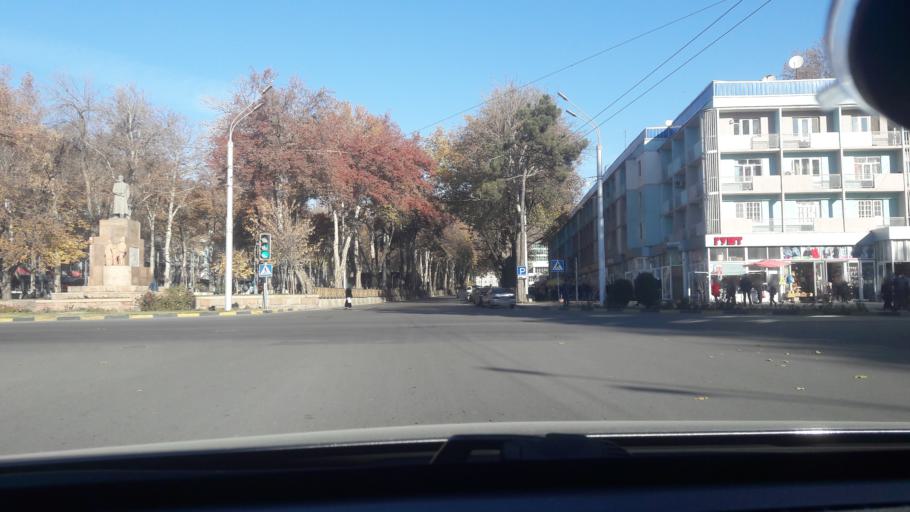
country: TJ
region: Dushanbe
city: Dushanbe
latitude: 38.5580
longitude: 68.7999
